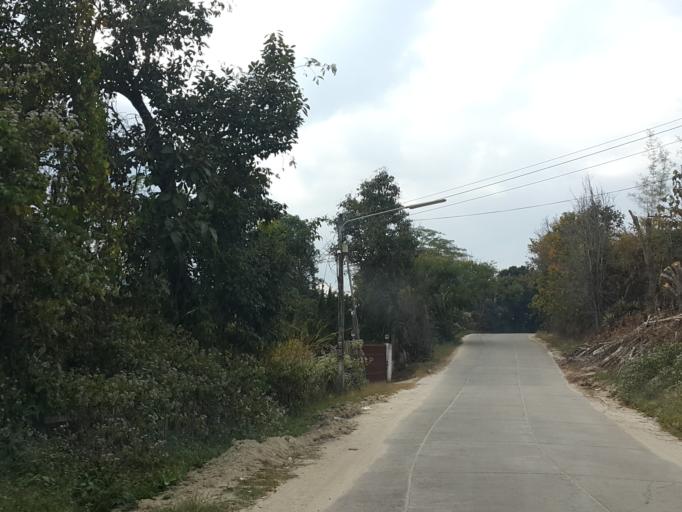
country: TH
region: Chiang Mai
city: Om Koi
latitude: 17.7975
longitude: 98.3537
